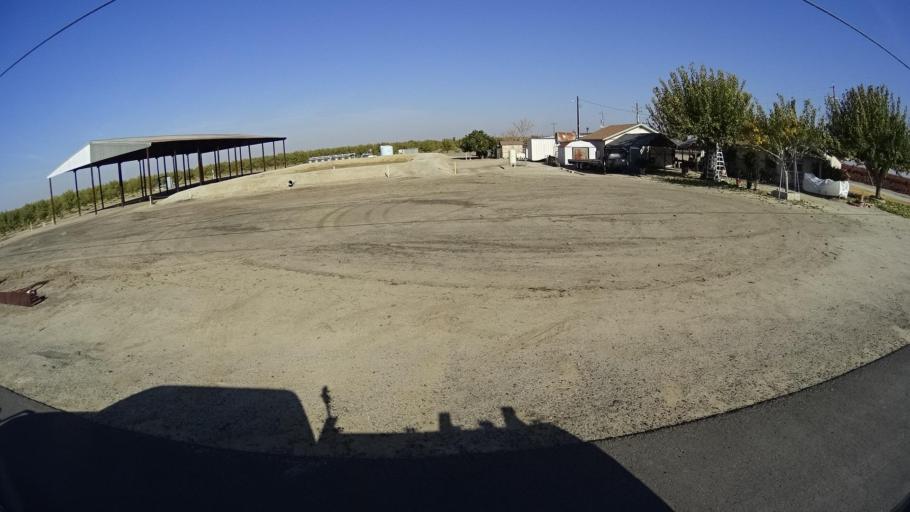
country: US
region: California
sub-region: Kern County
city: Delano
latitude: 35.7172
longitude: -119.3069
